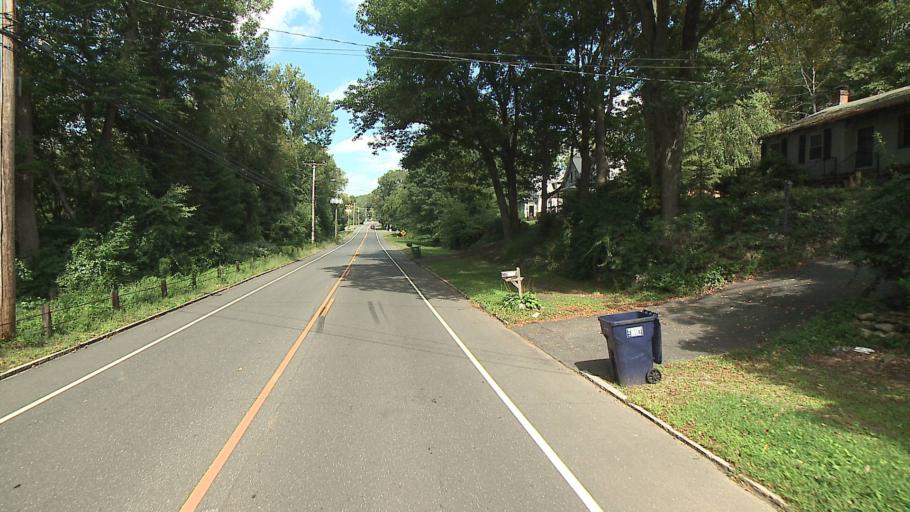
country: US
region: Connecticut
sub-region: New Haven County
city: Seymour
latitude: 41.3760
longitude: -73.0793
